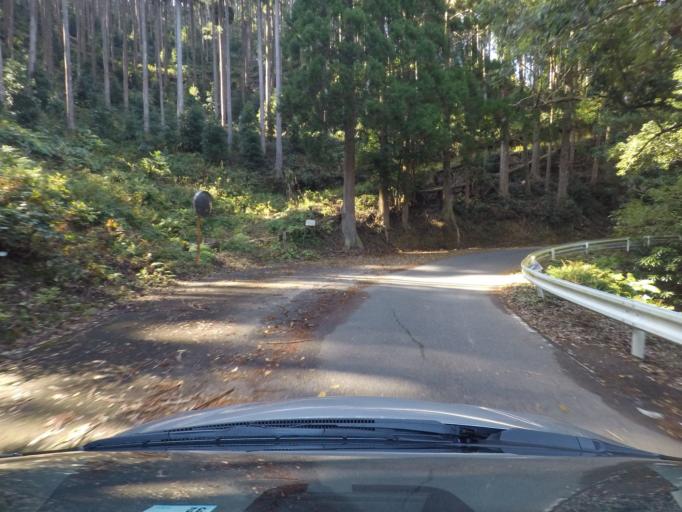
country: JP
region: Miyazaki
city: Kobayashi
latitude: 32.0233
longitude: 131.1815
